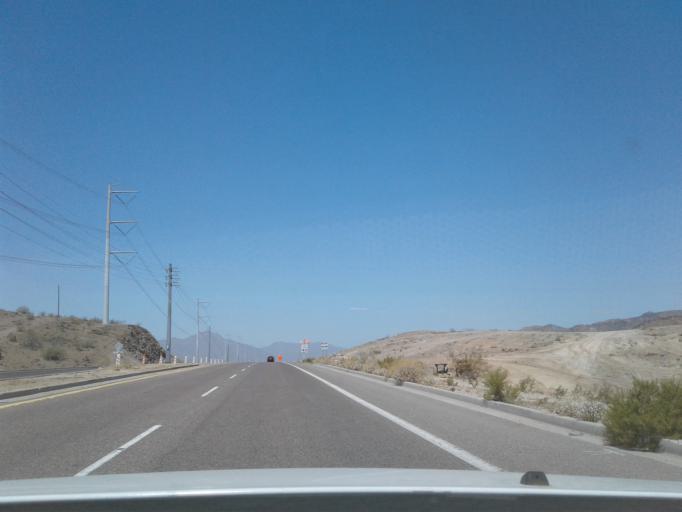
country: US
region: Arizona
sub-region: Maricopa County
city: Laveen
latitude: 33.2911
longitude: -112.0640
